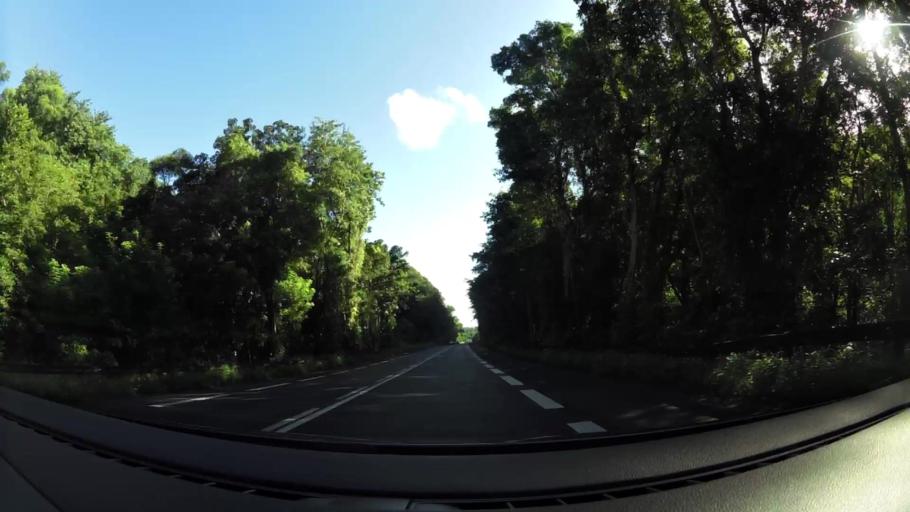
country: GP
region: Guadeloupe
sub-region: Guadeloupe
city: Petit-Canal
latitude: 16.3223
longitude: -61.4736
